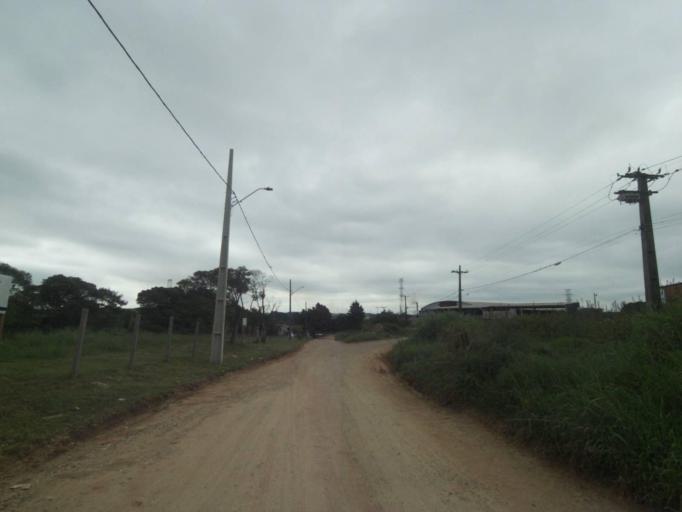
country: BR
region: Parana
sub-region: Araucaria
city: Araucaria
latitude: -25.5542
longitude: -49.3310
